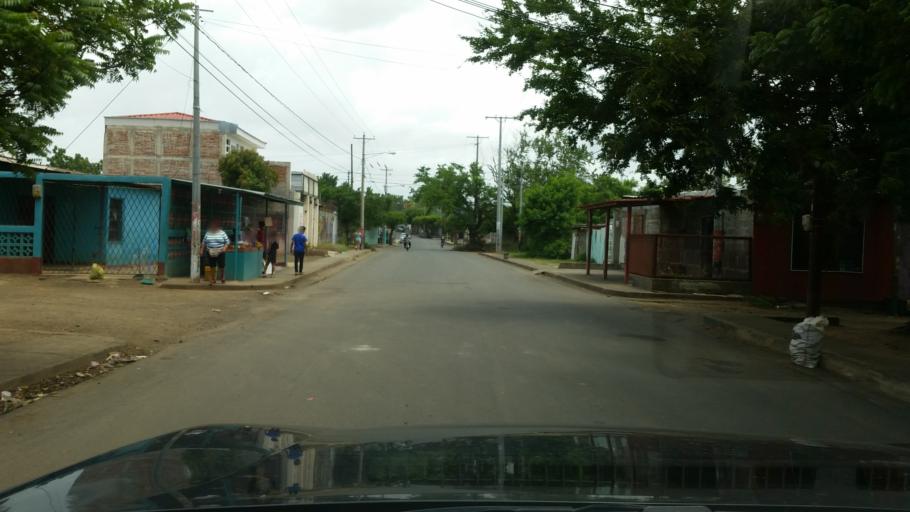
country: NI
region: Managua
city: Managua
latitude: 12.1367
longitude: -86.2137
